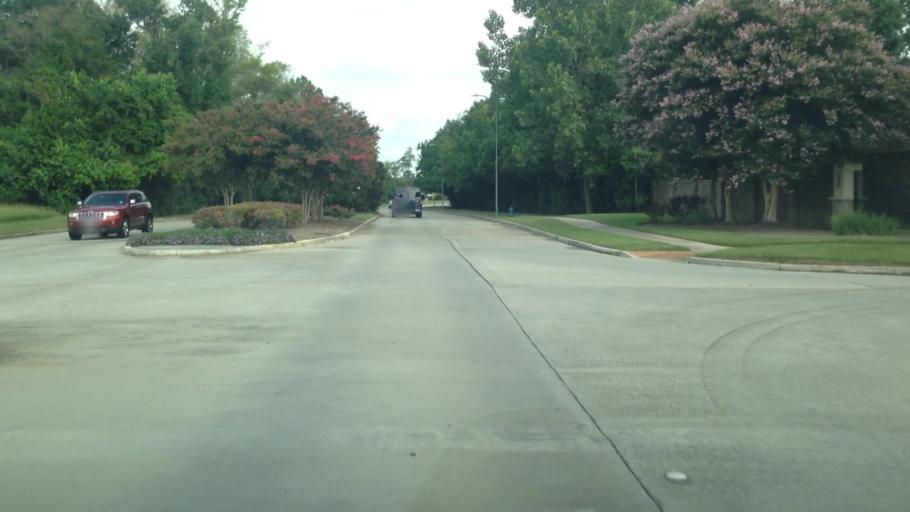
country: US
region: Texas
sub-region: Harris County
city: Atascocita
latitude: 29.9271
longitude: -95.1968
